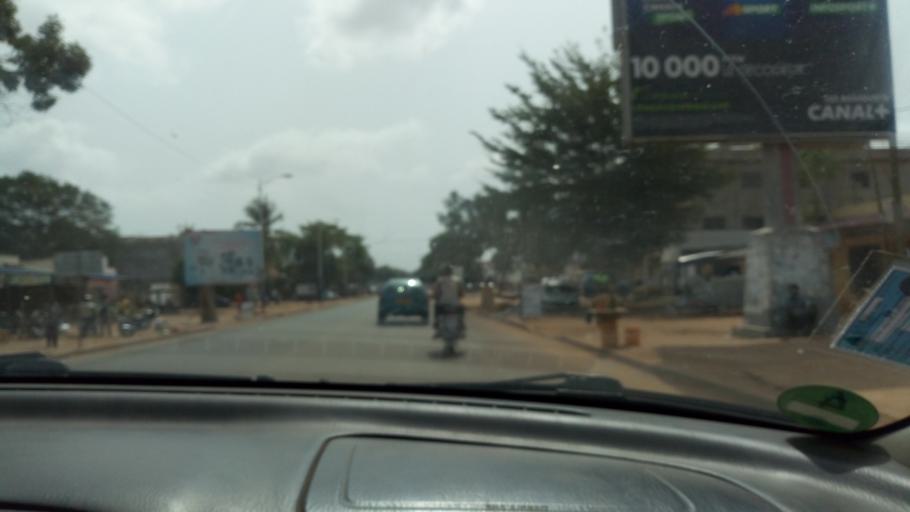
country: TG
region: Maritime
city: Lome
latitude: 6.1803
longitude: 1.1723
